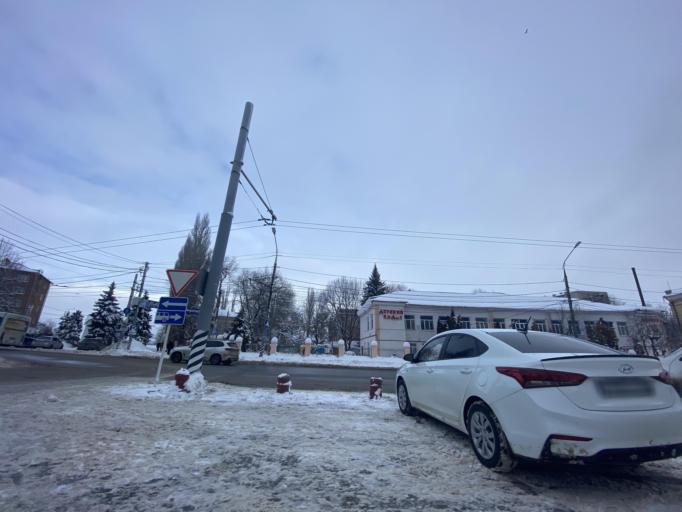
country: RU
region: Saratov
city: Engel's
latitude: 51.5034
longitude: 46.1179
